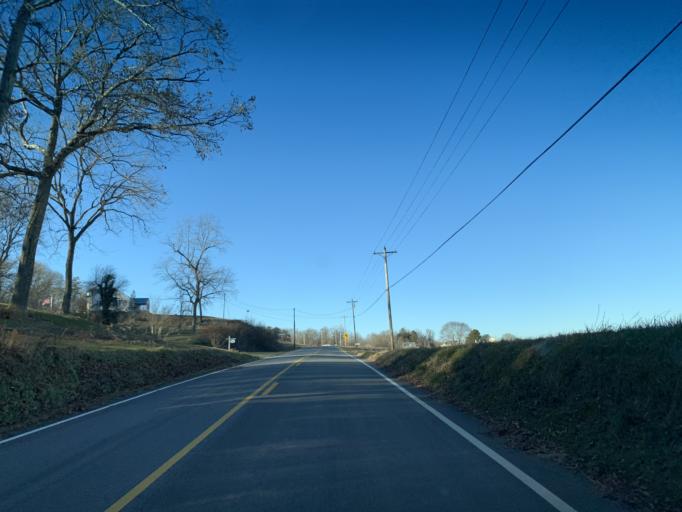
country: US
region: Maryland
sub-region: Saint Mary's County
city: Golden Beach
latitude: 38.4528
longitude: -76.6800
